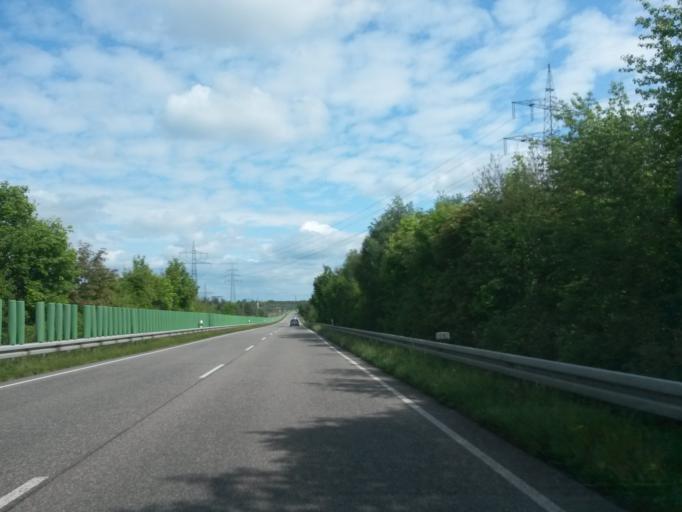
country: DE
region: Baden-Wuerttemberg
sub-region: Karlsruhe Region
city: Waghausel
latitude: 49.2153
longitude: 8.4999
